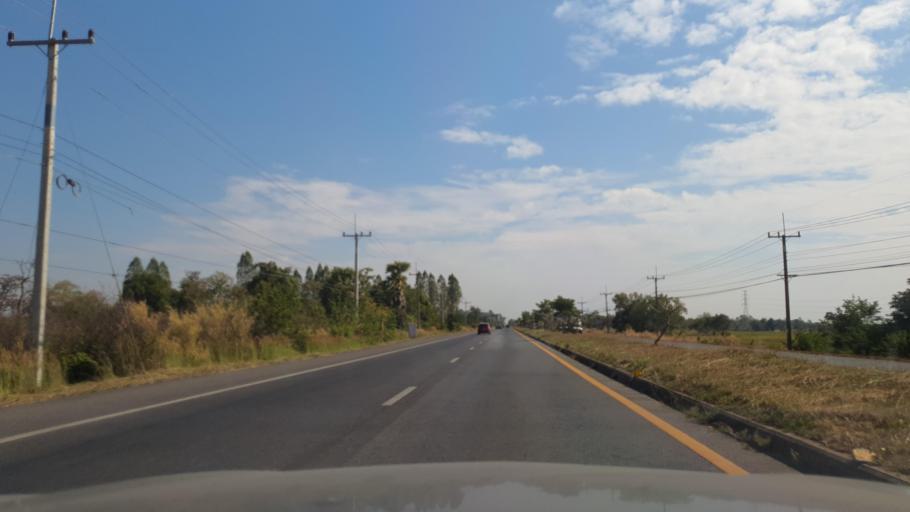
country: TH
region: Maha Sarakham
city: Kantharawichai
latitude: 16.3845
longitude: 103.2294
